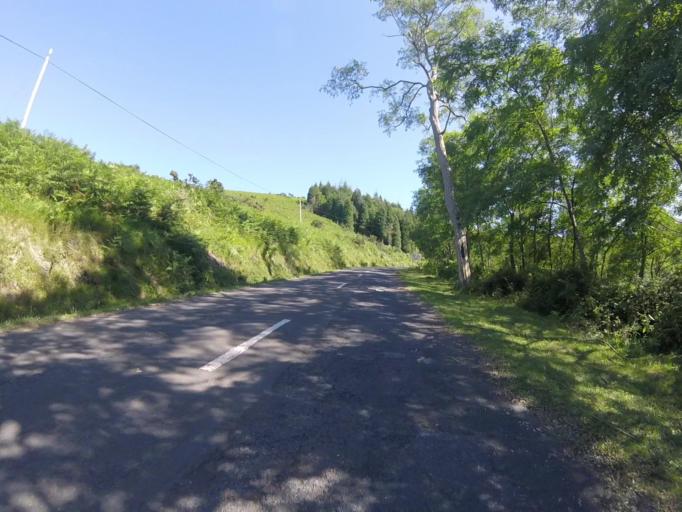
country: ES
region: Basque Country
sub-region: Provincia de Guipuzcoa
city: Irun
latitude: 43.2960
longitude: -1.8161
